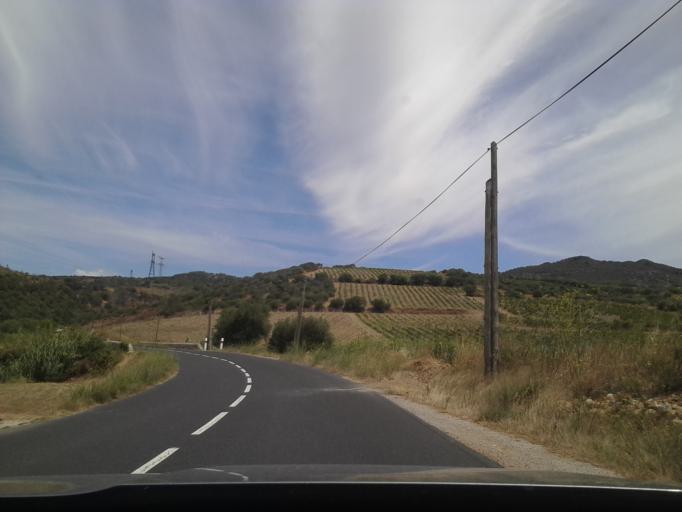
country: FR
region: Languedoc-Roussillon
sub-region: Departement des Pyrenees-Orientales
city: Millas
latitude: 42.7117
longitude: 2.6835
